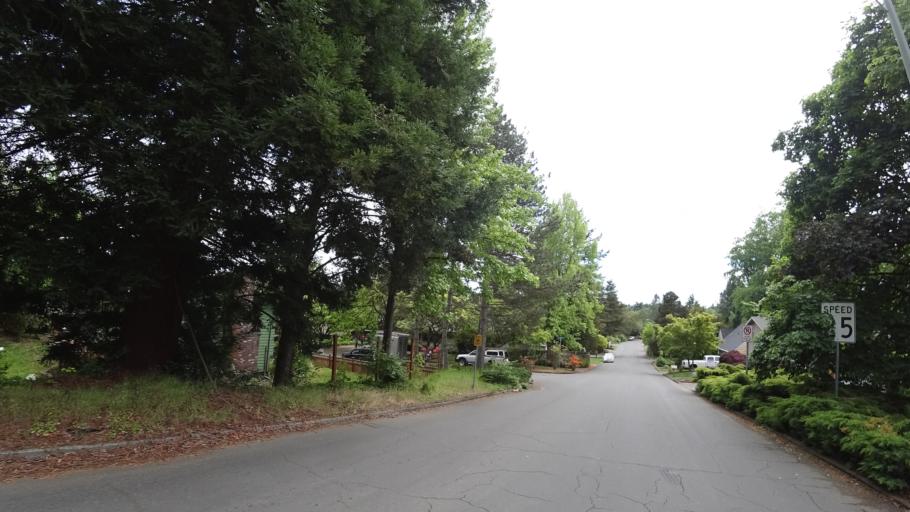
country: US
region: Oregon
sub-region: Washington County
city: Raleigh Hills
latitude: 45.4725
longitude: -122.7697
